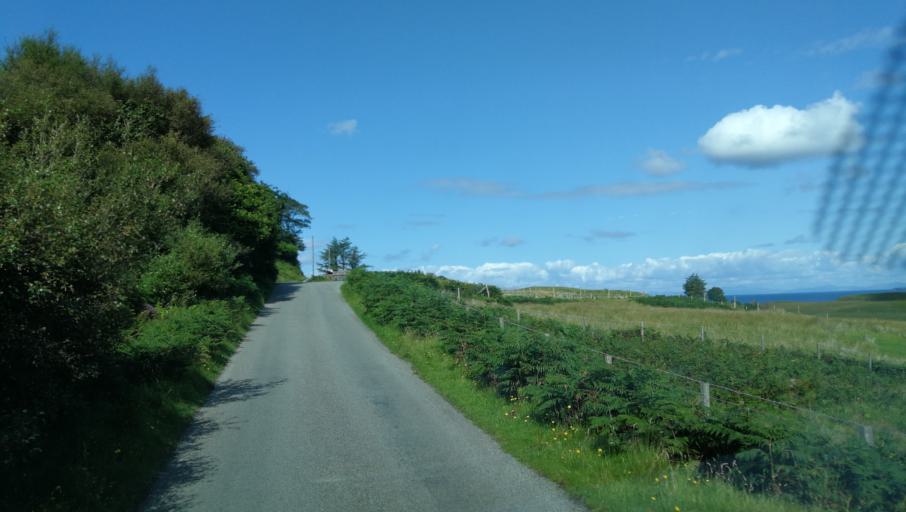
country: GB
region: Scotland
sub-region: Highland
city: Isle of Skye
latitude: 57.4508
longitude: -6.6556
